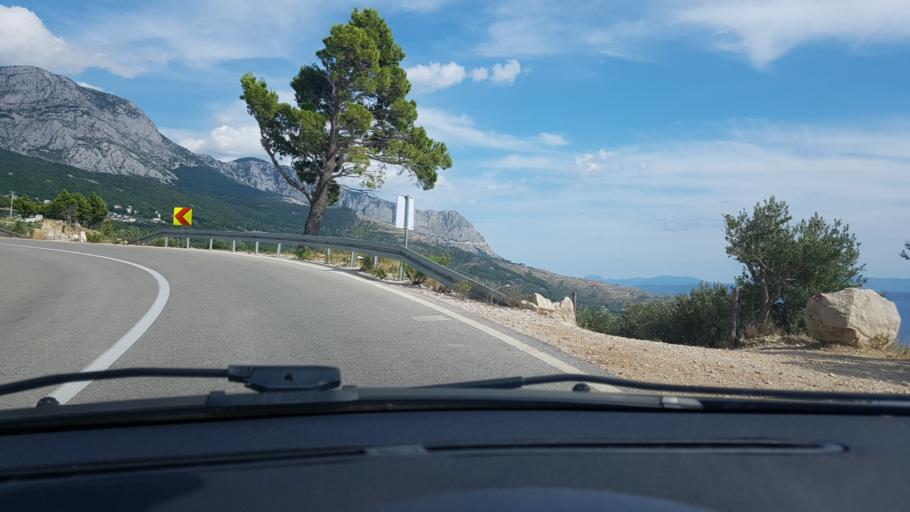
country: HR
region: Splitsko-Dalmatinska
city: Tucepi
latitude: 43.2782
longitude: 17.0492
